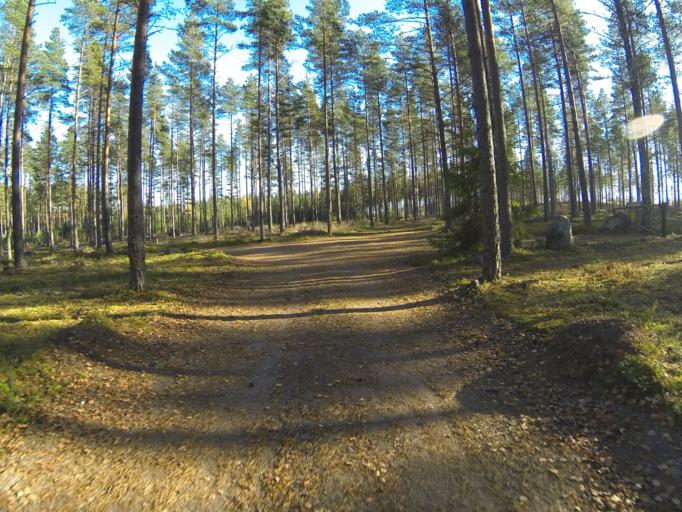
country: FI
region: Varsinais-Suomi
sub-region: Salo
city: Saerkisalo
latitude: 60.2134
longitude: 22.9848
